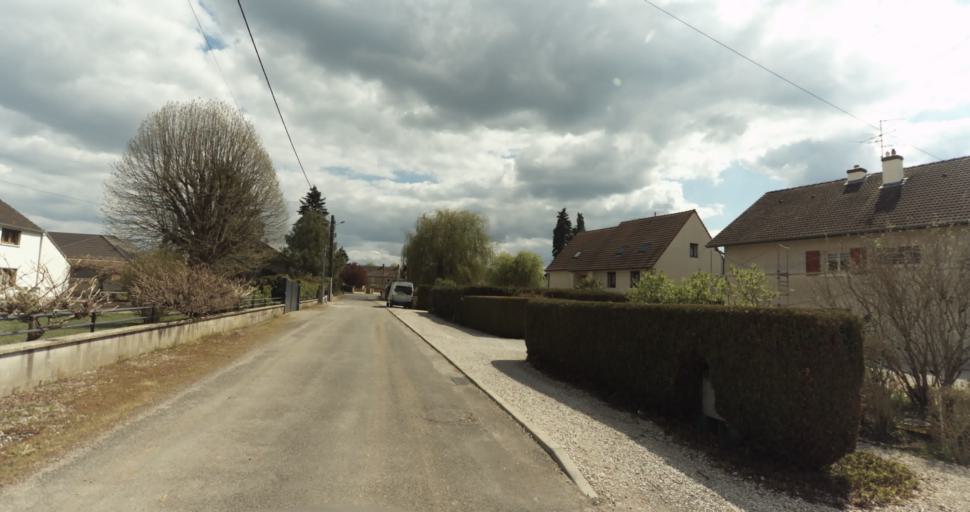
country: FR
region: Bourgogne
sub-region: Departement de la Cote-d'Or
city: Auxonne
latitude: 47.1835
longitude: 5.3953
